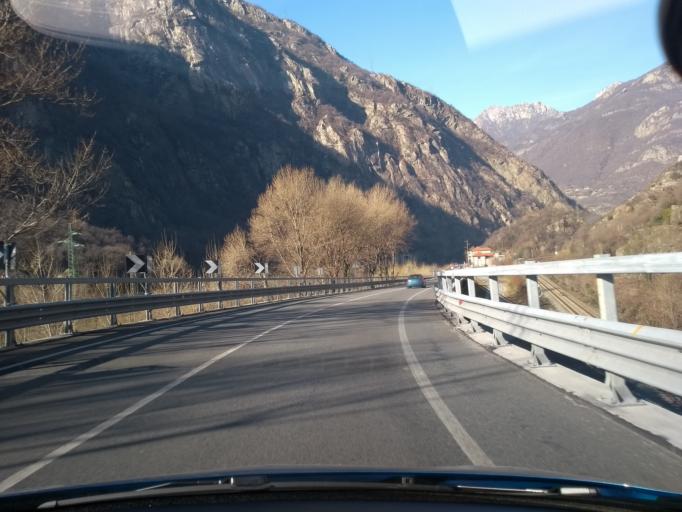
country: IT
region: Aosta Valley
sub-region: Valle d'Aosta
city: Bard
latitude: 45.6027
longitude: 7.7543
